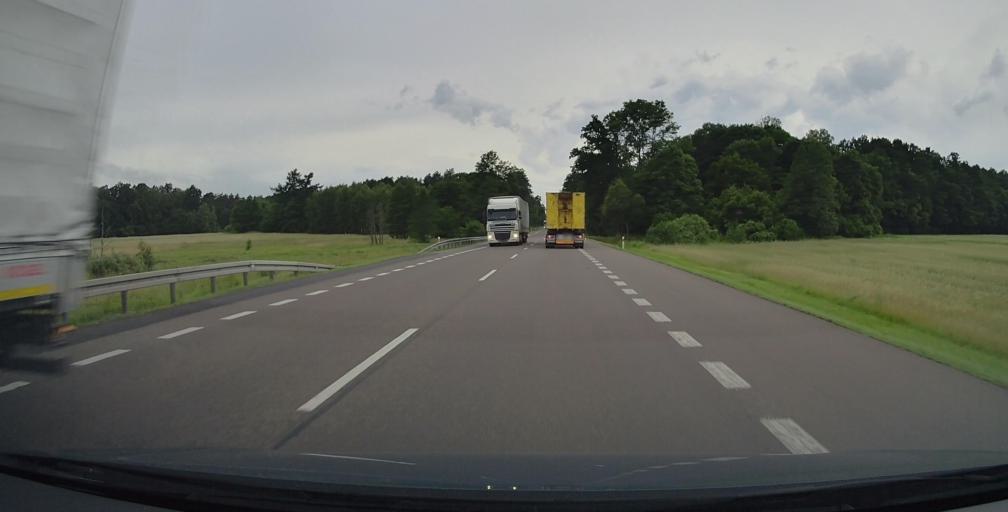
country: PL
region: Lublin Voivodeship
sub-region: Powiat bialski
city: Zalesie
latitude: 52.0368
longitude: 23.4472
